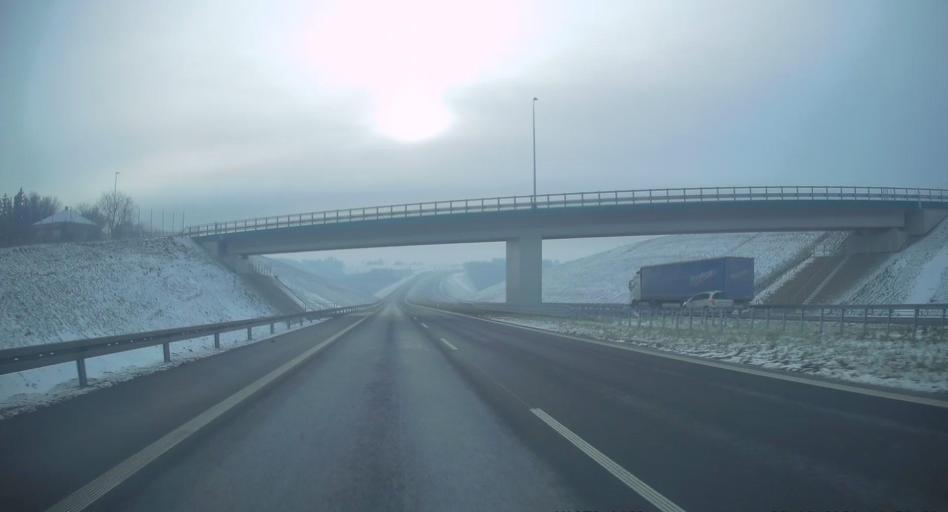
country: PL
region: Lesser Poland Voivodeship
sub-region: Powiat krakowski
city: Slomniki
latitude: 50.2652
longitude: 20.0204
